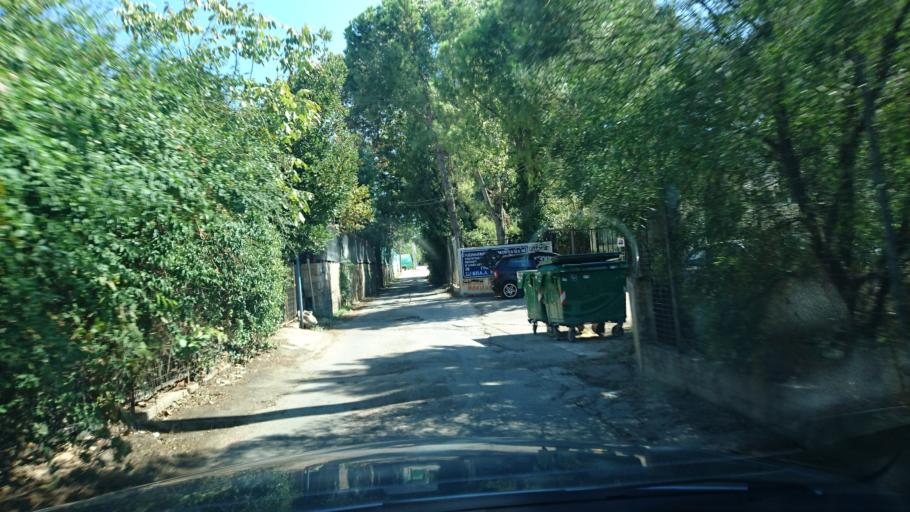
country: GR
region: Attica
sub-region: Nomarchia Athinas
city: Khalandrion
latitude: 38.0176
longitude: 23.8098
